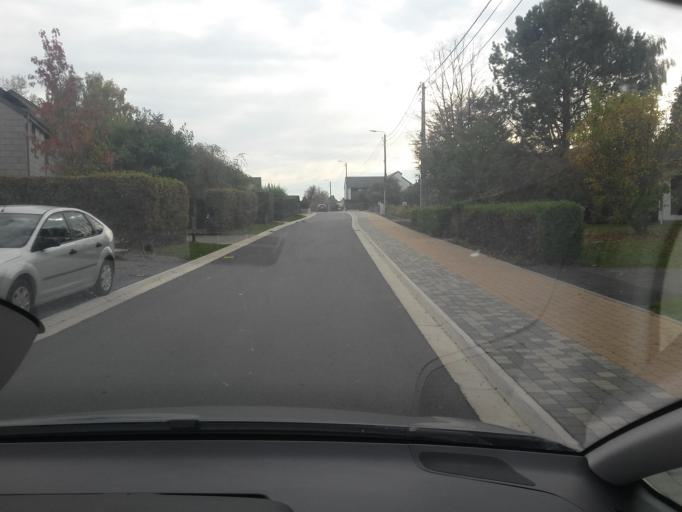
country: BE
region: Wallonia
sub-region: Province du Luxembourg
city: Arlon
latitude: 49.7045
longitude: 5.8198
